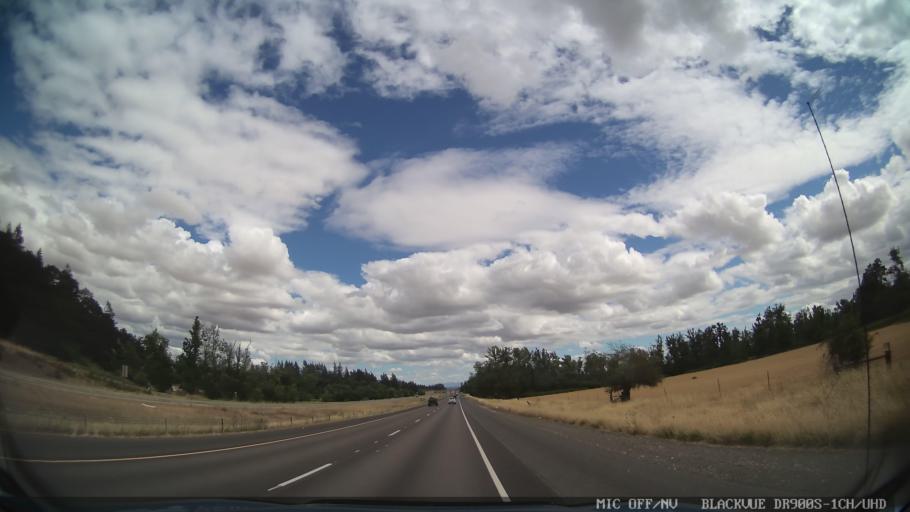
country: US
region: Oregon
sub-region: Marion County
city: Aumsville
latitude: 44.8596
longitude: -122.8793
